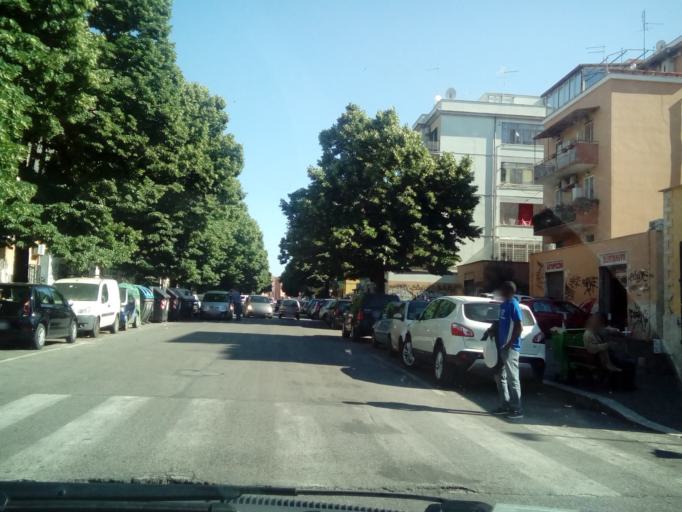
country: IT
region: Latium
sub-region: Citta metropolitana di Roma Capitale
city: Rome
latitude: 41.8906
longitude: 12.5665
